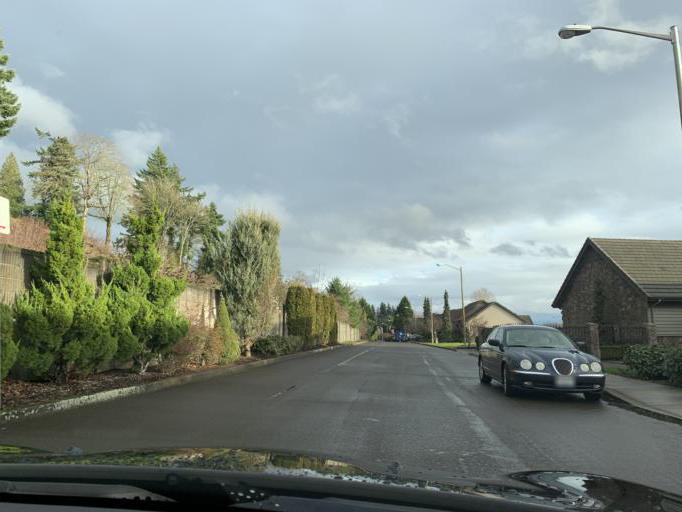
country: US
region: Washington
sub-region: Clark County
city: Mill Plain
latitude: 45.5902
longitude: -122.5135
